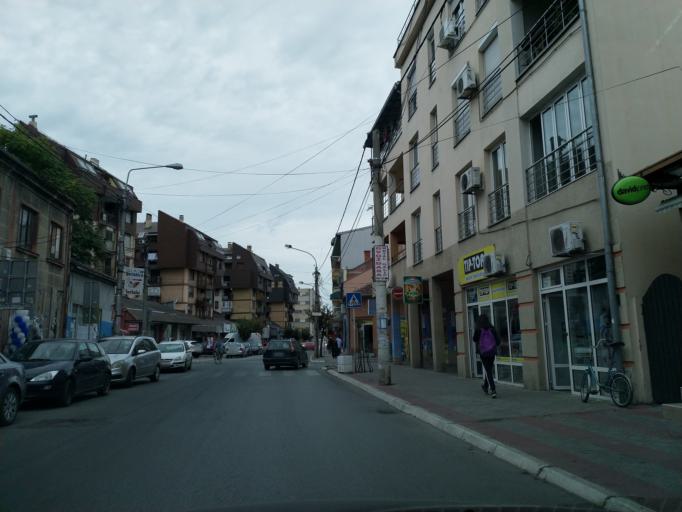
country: RS
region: Central Serbia
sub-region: Pomoravski Okrug
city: Jagodina
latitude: 43.9812
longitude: 21.2568
